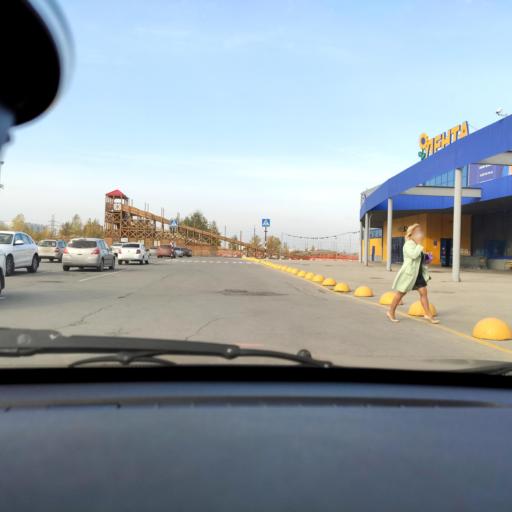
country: RU
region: Samara
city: Tol'yatti
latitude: 53.5485
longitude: 49.3601
